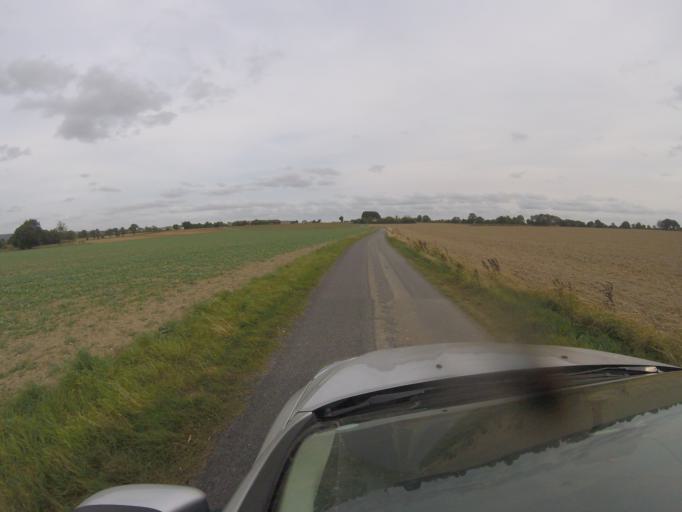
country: FR
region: Lower Normandy
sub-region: Departement de la Manche
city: Le Val-Saint-Pere
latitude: 48.6293
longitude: -1.3967
